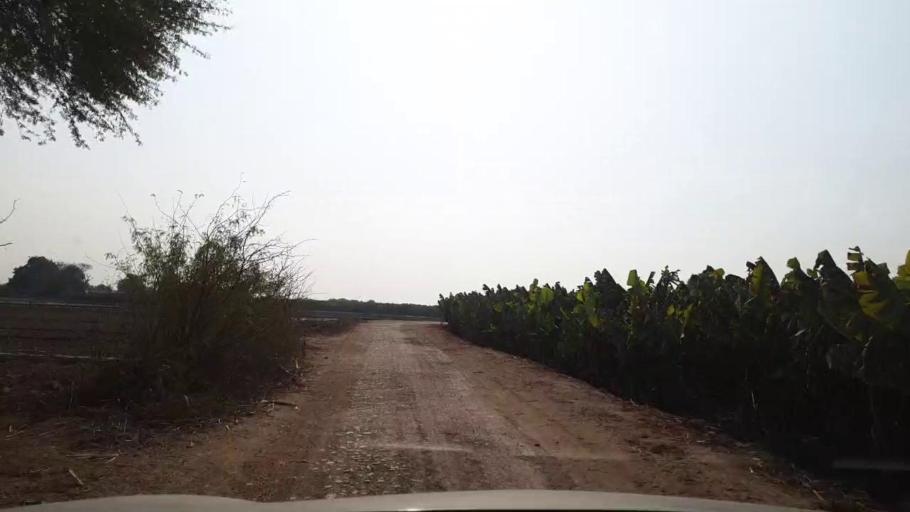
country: PK
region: Sindh
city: Tando Allahyar
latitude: 25.5531
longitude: 68.7828
